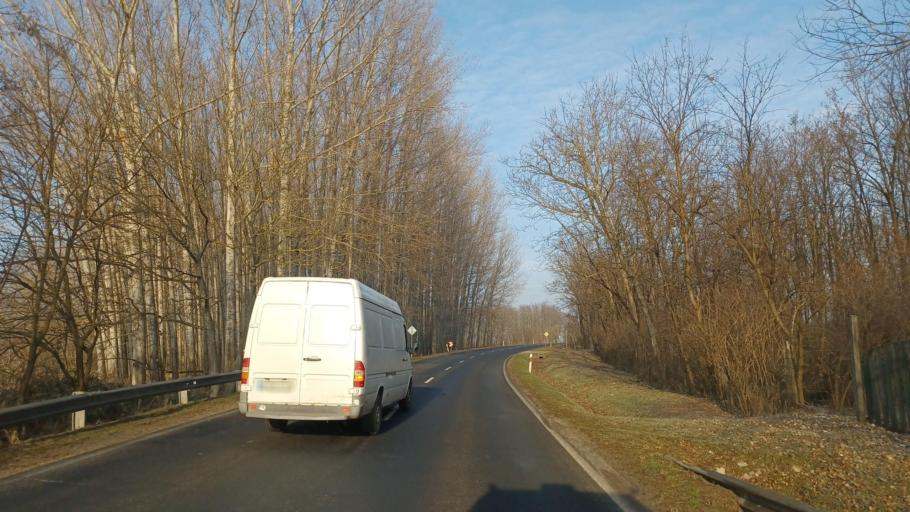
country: HU
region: Fejer
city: Cece
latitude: 46.7462
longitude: 18.6457
